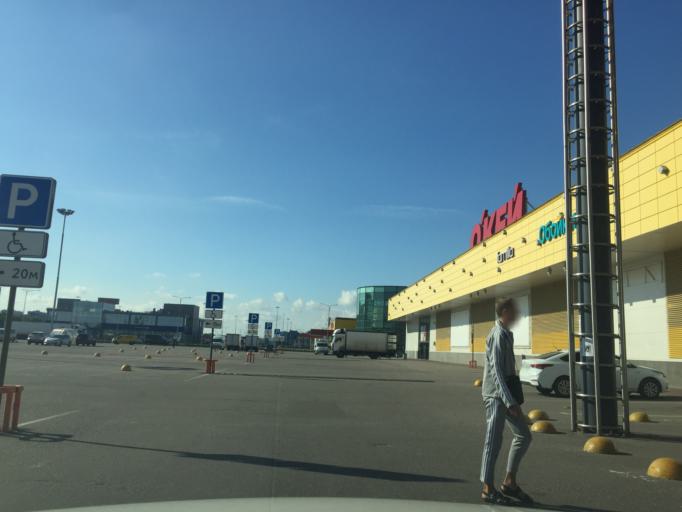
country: RU
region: St.-Petersburg
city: Kupchino
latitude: 59.8279
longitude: 30.3173
